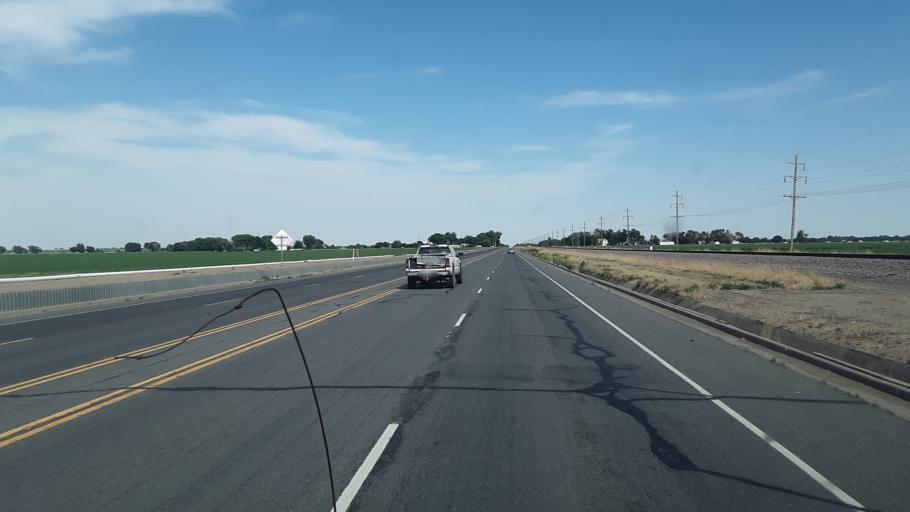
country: US
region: Colorado
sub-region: Otero County
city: Rocky Ford
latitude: 38.0713
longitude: -103.7653
